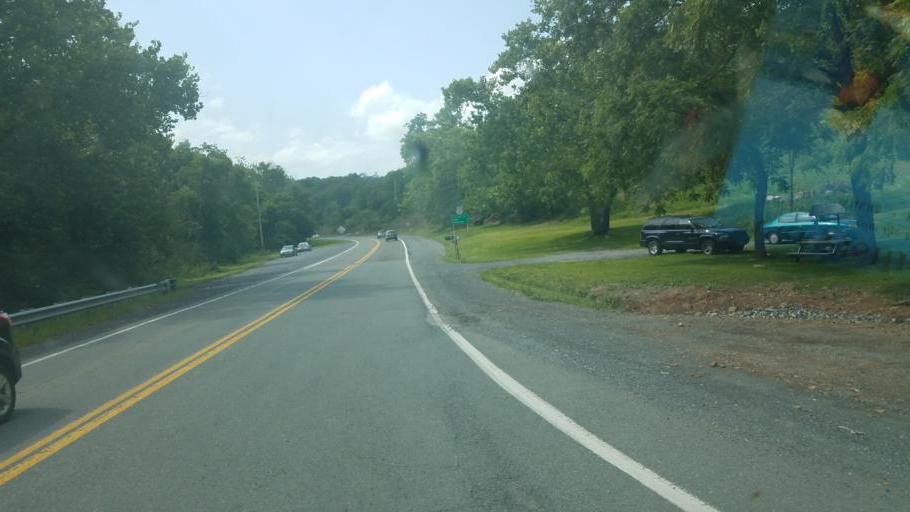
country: US
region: Virginia
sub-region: Frederick County
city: Shawnee Land
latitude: 39.3405
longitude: -78.3066
